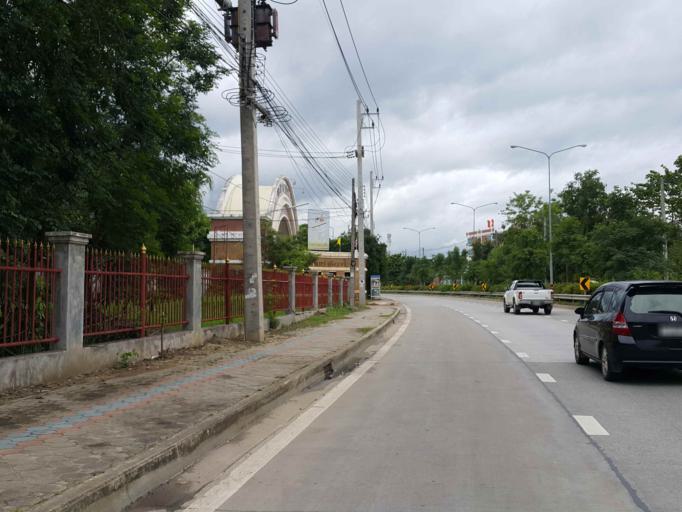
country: TH
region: Chiang Mai
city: San Sai
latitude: 18.8448
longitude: 98.9948
